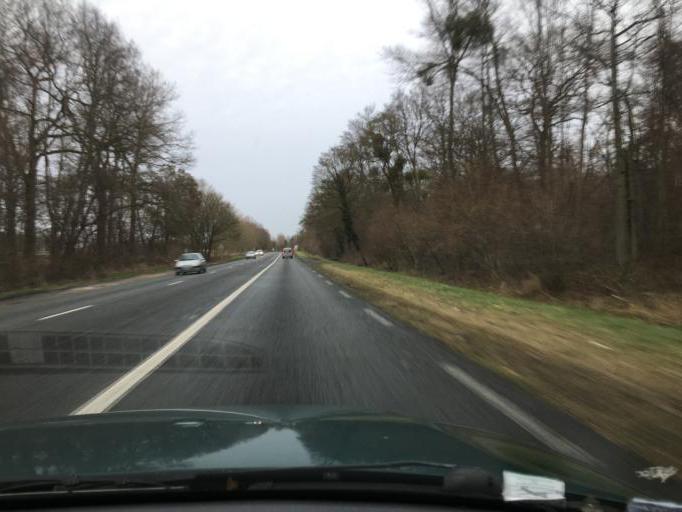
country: FR
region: Picardie
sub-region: Departement de l'Oise
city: Senlis
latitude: 49.1867
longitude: 2.5708
